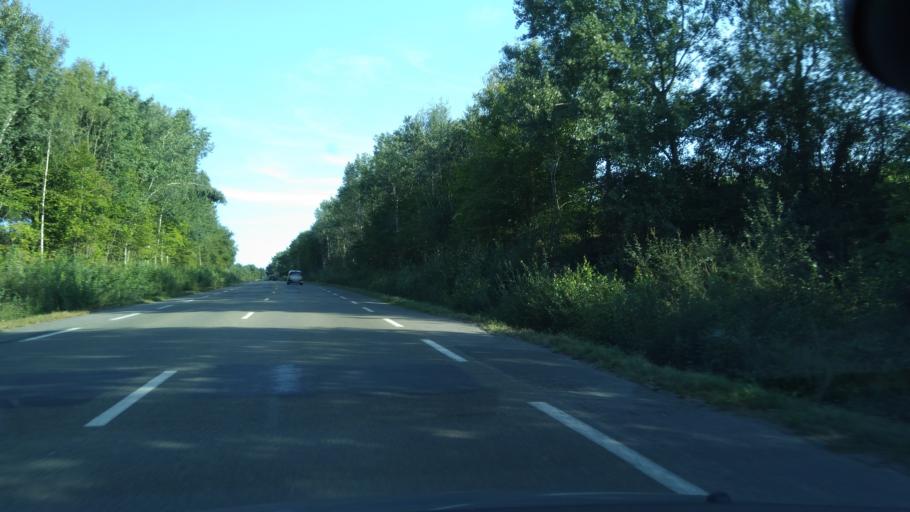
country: FR
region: Pays de la Loire
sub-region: Departement de la Mayenne
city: Entrammes
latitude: 47.9931
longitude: -0.7179
